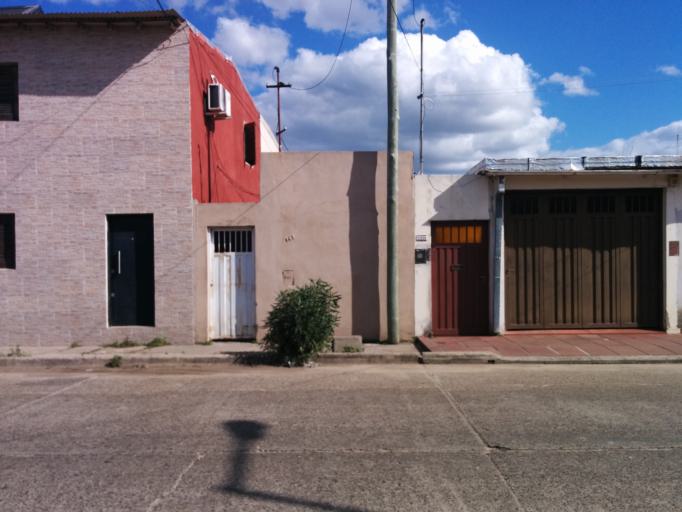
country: AR
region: Entre Rios
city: Concordia
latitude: -31.3864
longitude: -58.0200
